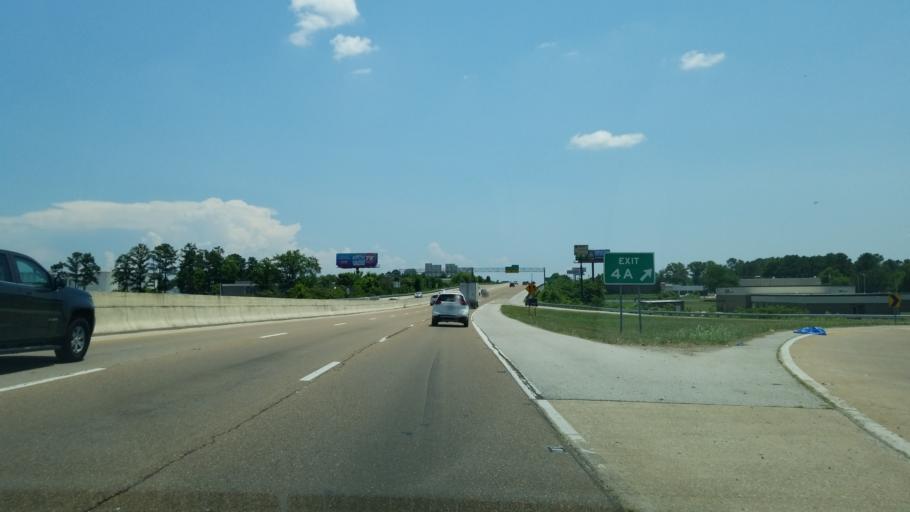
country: US
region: Tennessee
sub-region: Hamilton County
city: East Chattanooga
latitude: 35.0748
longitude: -85.1990
